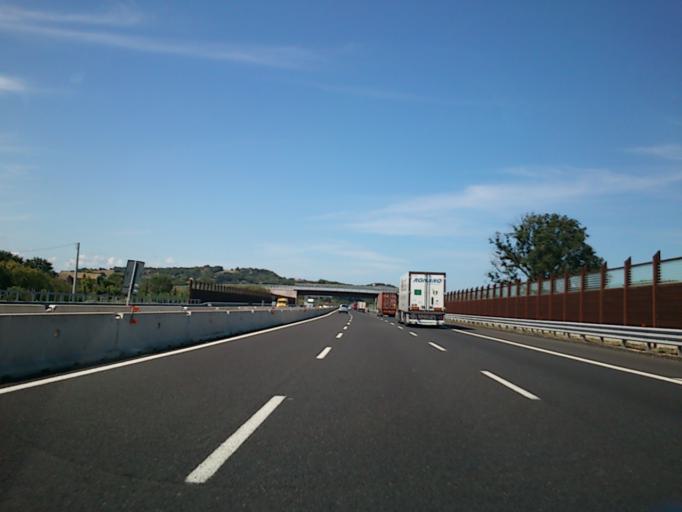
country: IT
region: The Marches
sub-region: Provincia di Pesaro e Urbino
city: Centinarola
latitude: 43.8396
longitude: 12.9840
